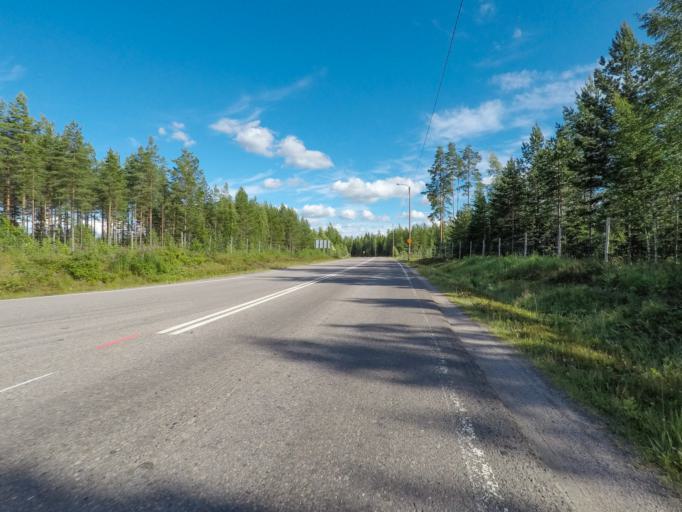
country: FI
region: South Karelia
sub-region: Lappeenranta
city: Joutseno
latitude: 61.1483
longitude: 28.6164
